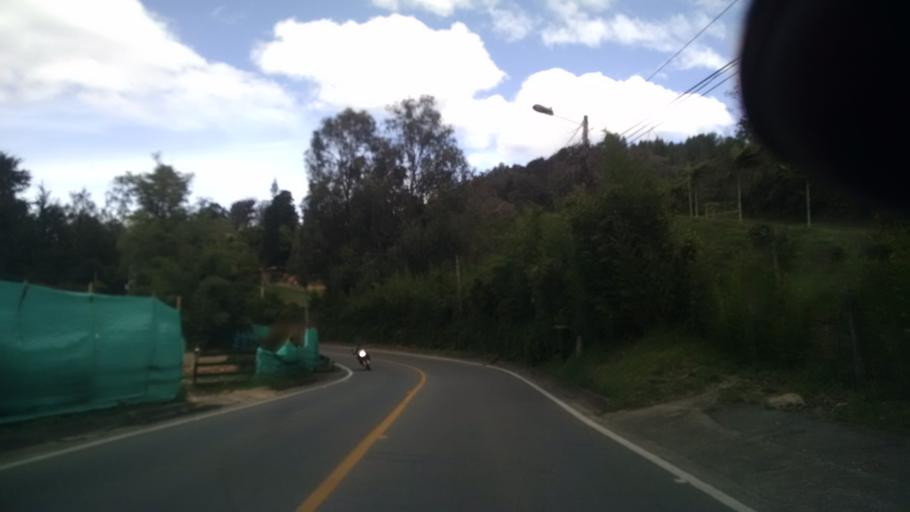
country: CO
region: Antioquia
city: El Retiro
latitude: 6.0815
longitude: -75.4944
